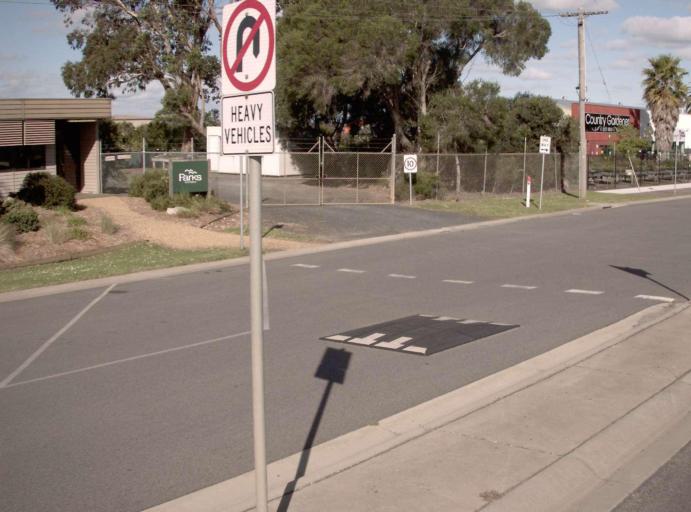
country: AU
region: Victoria
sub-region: Bass Coast
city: North Wonthaggi
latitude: -38.6059
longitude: 145.6036
